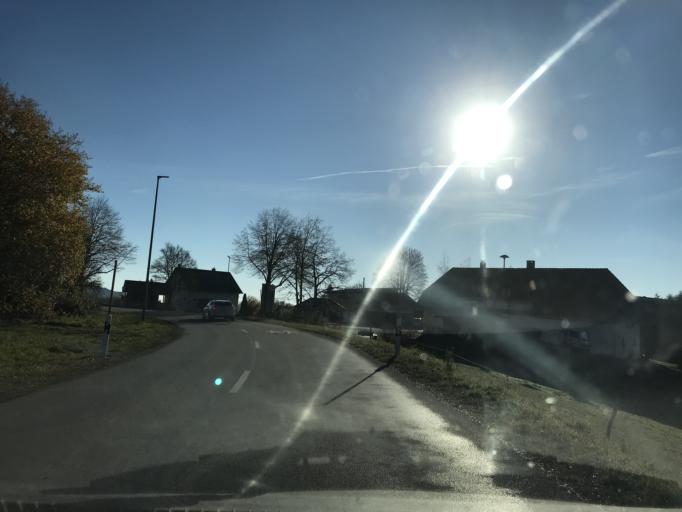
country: DE
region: Baden-Wuerttemberg
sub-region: Freiburg Region
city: Rickenbach
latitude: 47.6372
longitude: 7.9749
